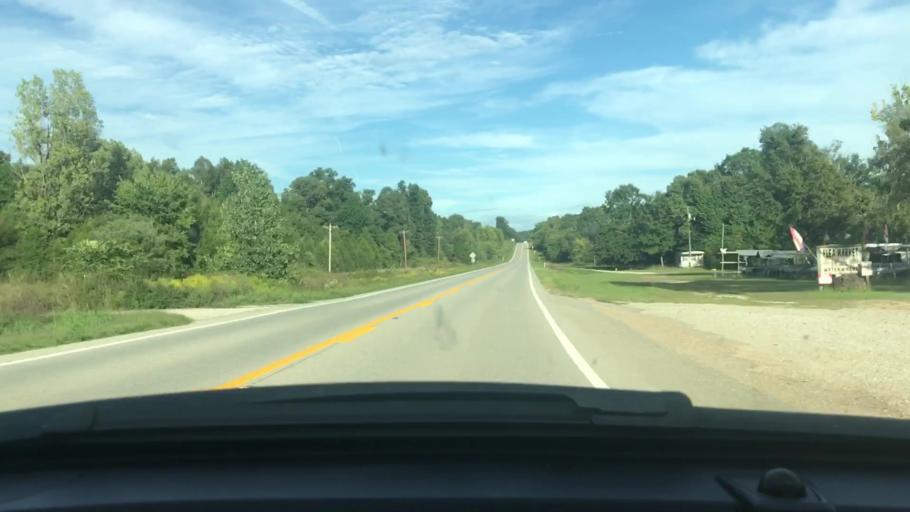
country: US
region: Arkansas
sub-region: Sharp County
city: Cherokee Village
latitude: 36.2747
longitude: -91.3497
